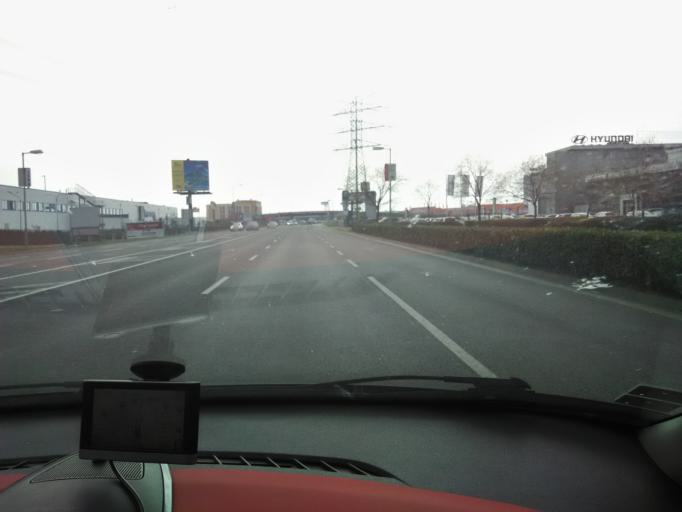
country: SK
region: Bratislavsky
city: Bratislava
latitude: 48.1659
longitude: 17.1785
